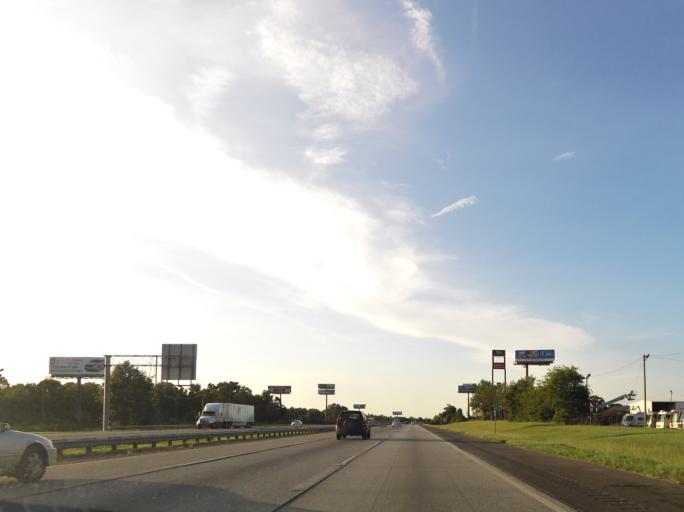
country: US
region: Georgia
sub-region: Peach County
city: Byron
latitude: 32.6682
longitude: -83.7444
